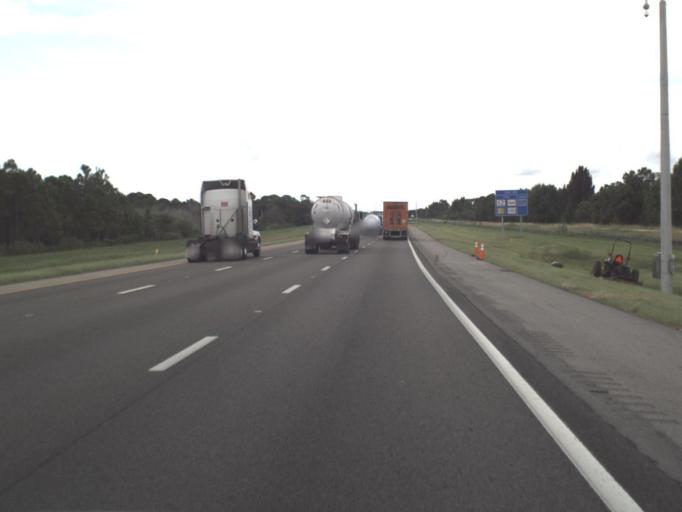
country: US
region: Florida
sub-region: Sarasota County
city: Nokomis
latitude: 27.1525
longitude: -82.4214
